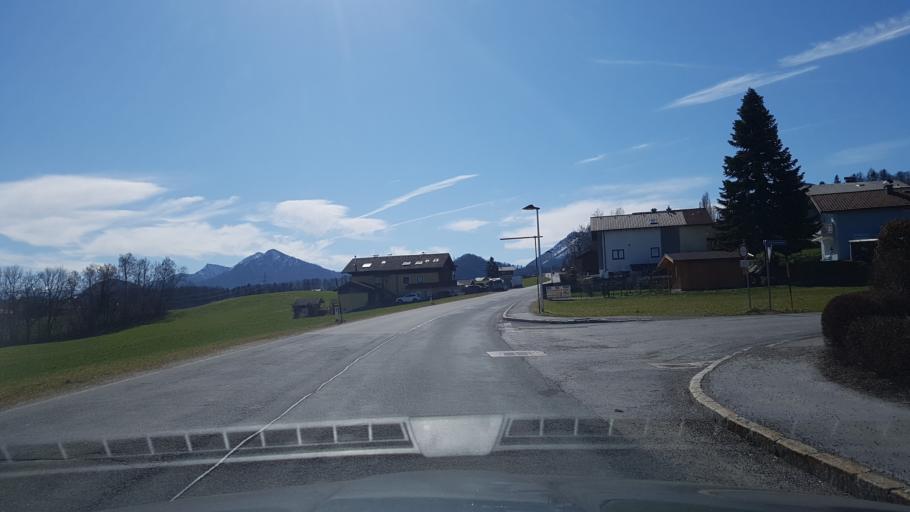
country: AT
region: Salzburg
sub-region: Politischer Bezirk Salzburg-Umgebung
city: Koppl
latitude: 47.8158
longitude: 13.1536
